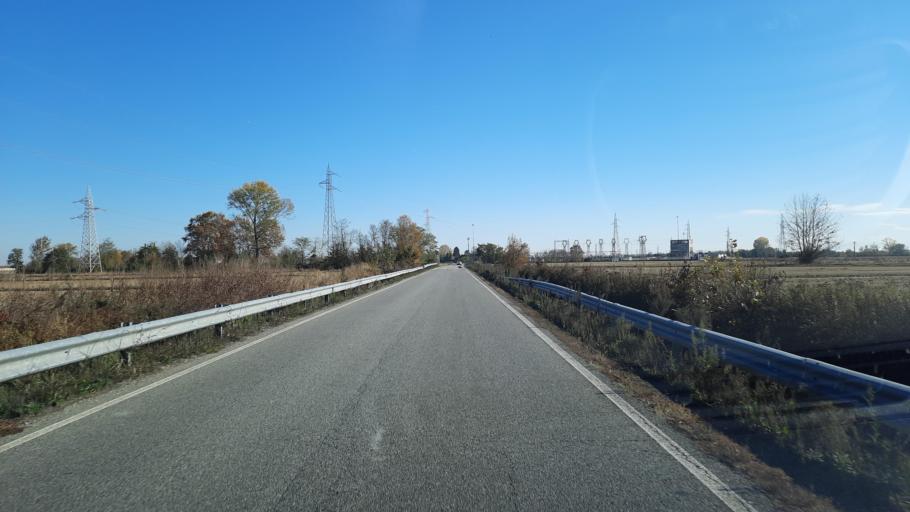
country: IT
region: Piedmont
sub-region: Provincia di Alessandria
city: Balzola
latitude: 45.1867
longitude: 8.4218
